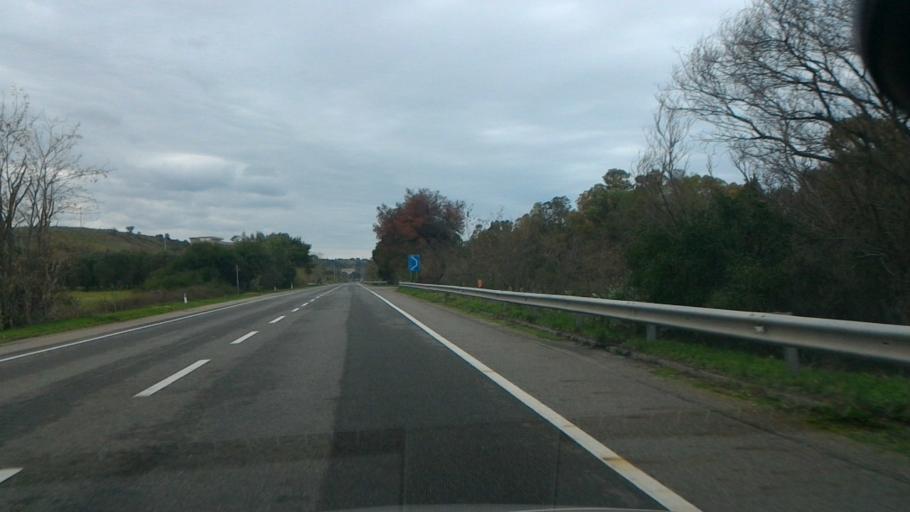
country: IT
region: Calabria
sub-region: Provincia di Crotone
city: Torretta
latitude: 39.4303
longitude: 17.0625
